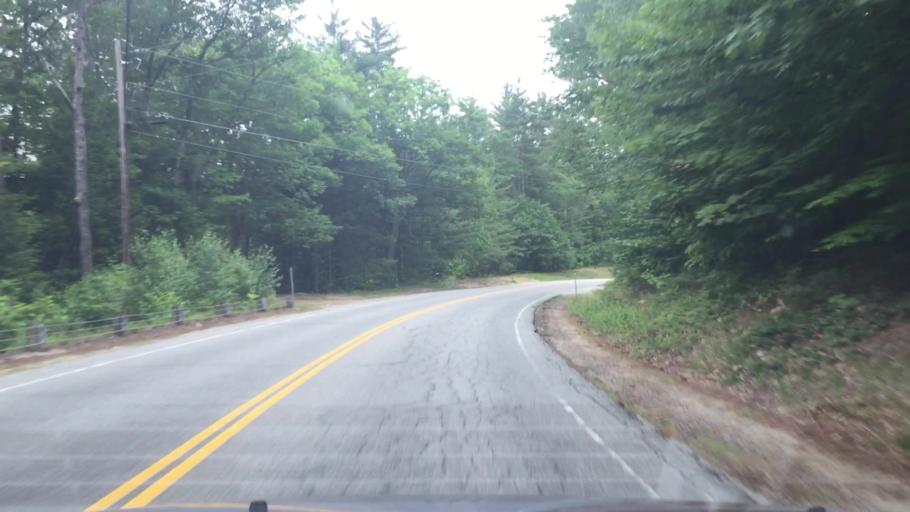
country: US
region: New Hampshire
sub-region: Carroll County
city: North Conway
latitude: 44.0826
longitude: -71.1638
